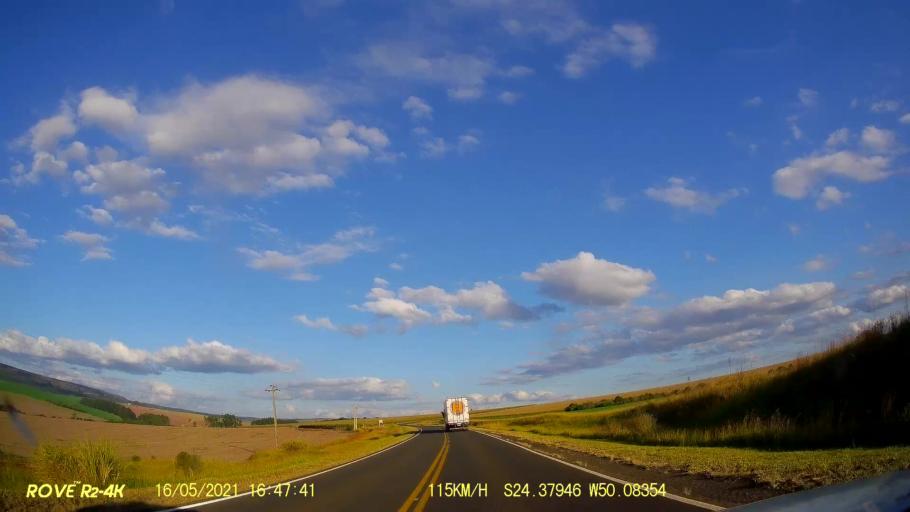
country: BR
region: Parana
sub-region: Pirai Do Sul
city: Pirai do Sul
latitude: -24.3796
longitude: -50.0832
